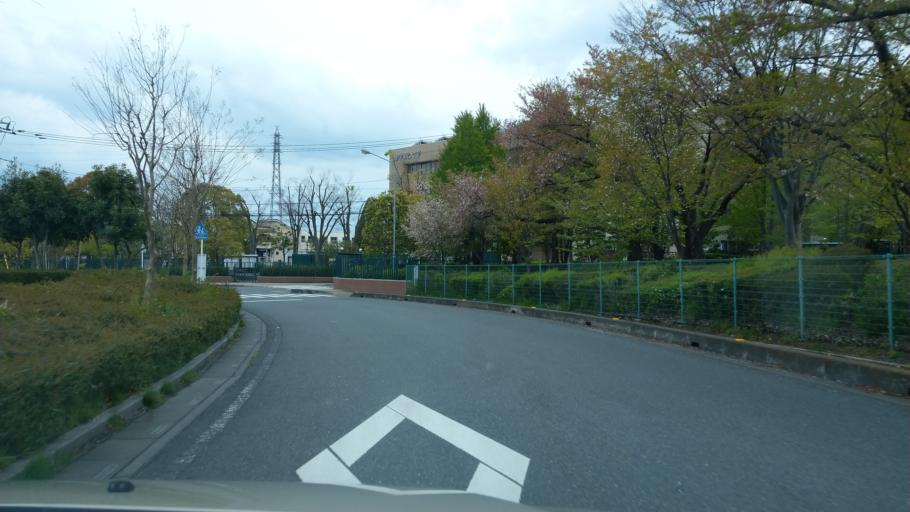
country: JP
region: Saitama
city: Ageoshimo
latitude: 35.9389
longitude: 139.5974
